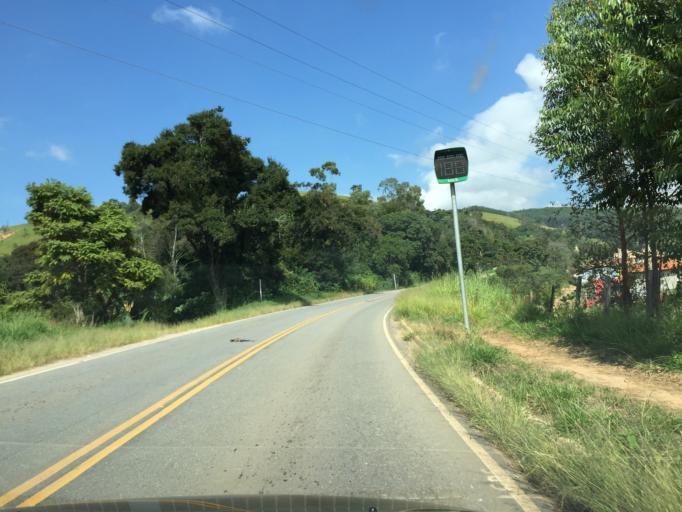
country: BR
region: Minas Gerais
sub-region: Passa Quatro
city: Passa Quatro
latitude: -22.3906
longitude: -44.9624
